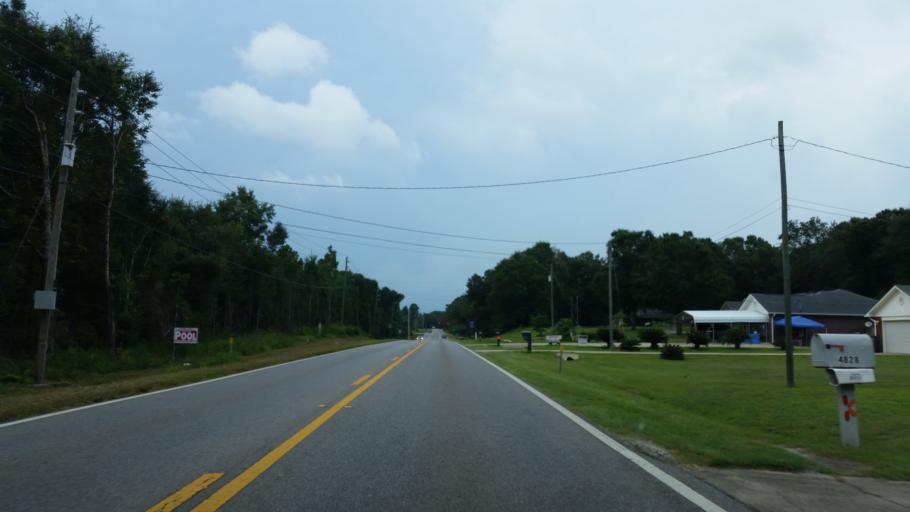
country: US
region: Florida
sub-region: Santa Rosa County
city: Pace
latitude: 30.6124
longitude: -87.1612
